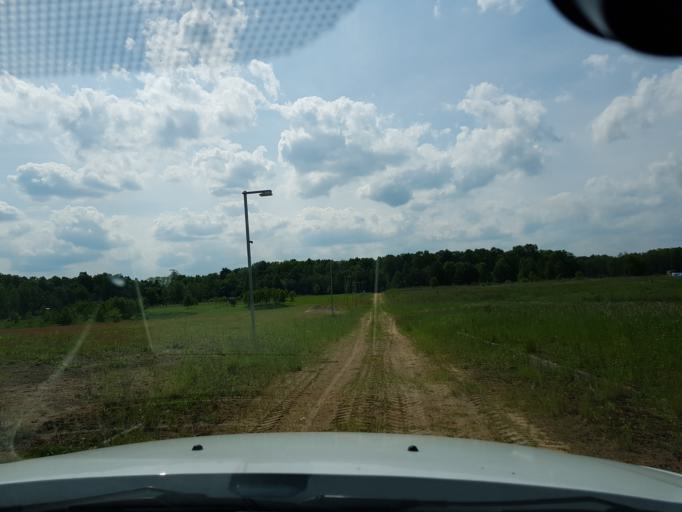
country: PL
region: West Pomeranian Voivodeship
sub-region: Powiat stargardzki
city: Insko
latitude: 53.4817
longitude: 15.6031
